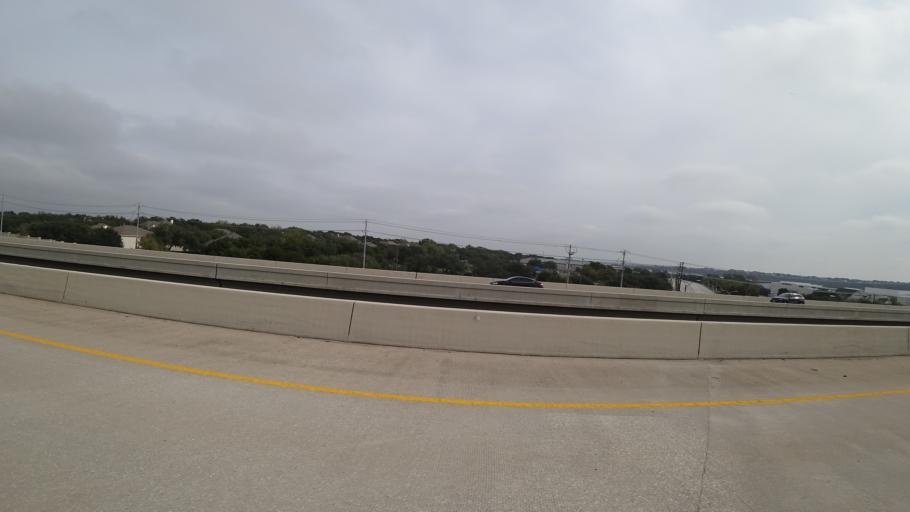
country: US
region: Texas
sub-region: Williamson County
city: Cedar Park
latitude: 30.5037
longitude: -97.8092
